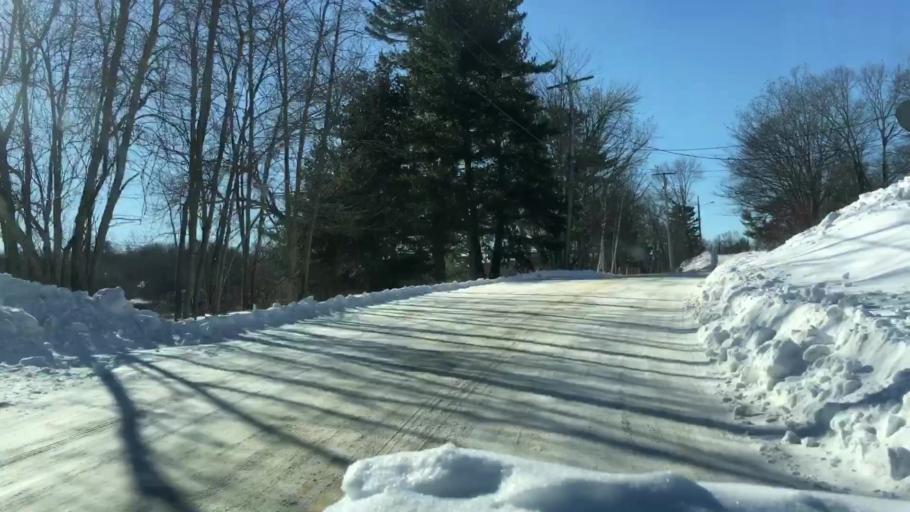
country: US
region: Maine
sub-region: Cumberland County
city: Brunswick
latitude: 43.9183
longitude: -69.9738
